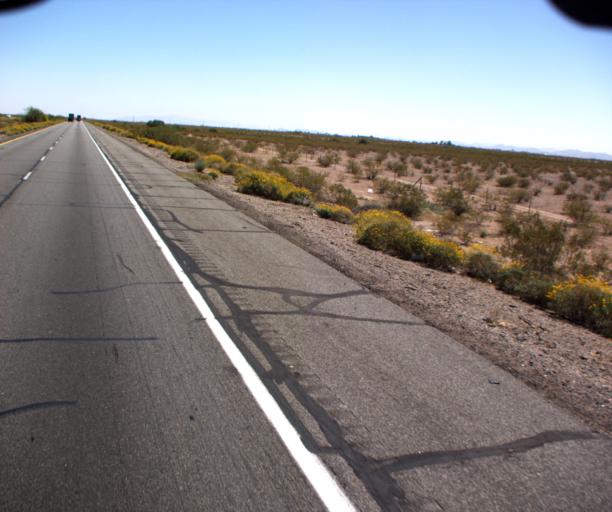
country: US
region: Arizona
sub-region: Maricopa County
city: Buckeye
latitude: 33.4773
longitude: -112.8477
